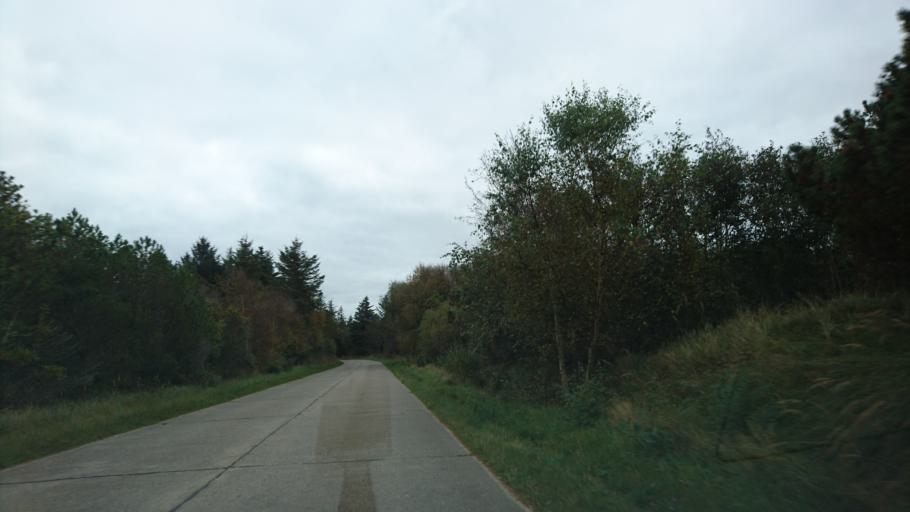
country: DK
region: North Denmark
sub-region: Frederikshavn Kommune
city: Skagen
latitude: 57.6564
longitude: 10.4144
